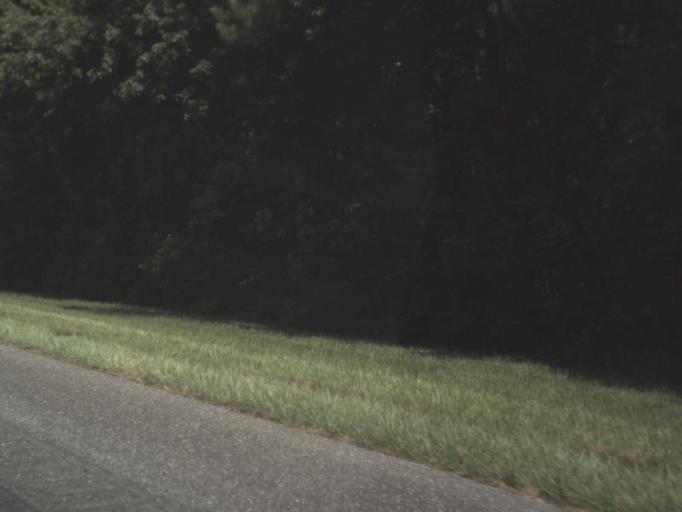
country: US
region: Florida
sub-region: Jefferson County
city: Monticello
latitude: 30.4454
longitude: -83.7190
